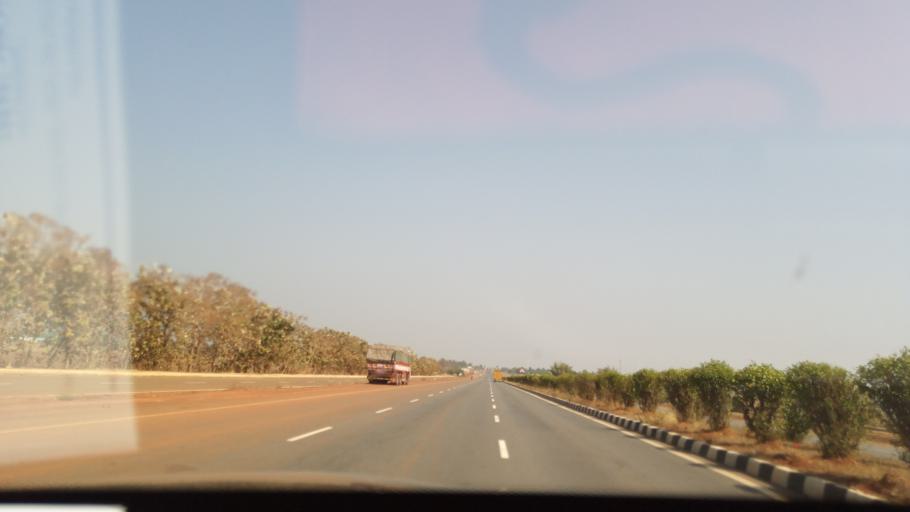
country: IN
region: Karnataka
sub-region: Haveri
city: Shiggaon
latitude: 15.0855
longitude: 75.1521
